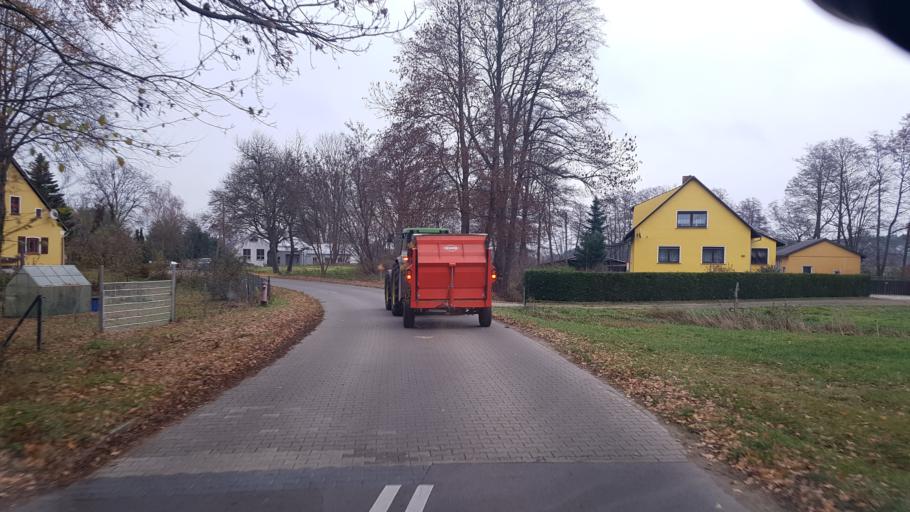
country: DE
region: Brandenburg
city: Schenkendobern
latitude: 51.9626
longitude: 14.6512
